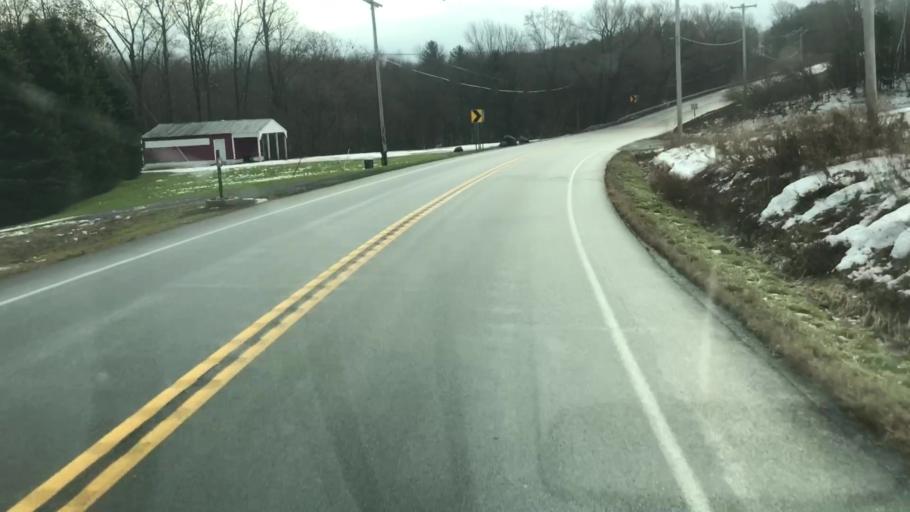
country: US
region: New York
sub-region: Cayuga County
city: Moravia
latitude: 42.8303
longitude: -76.3515
